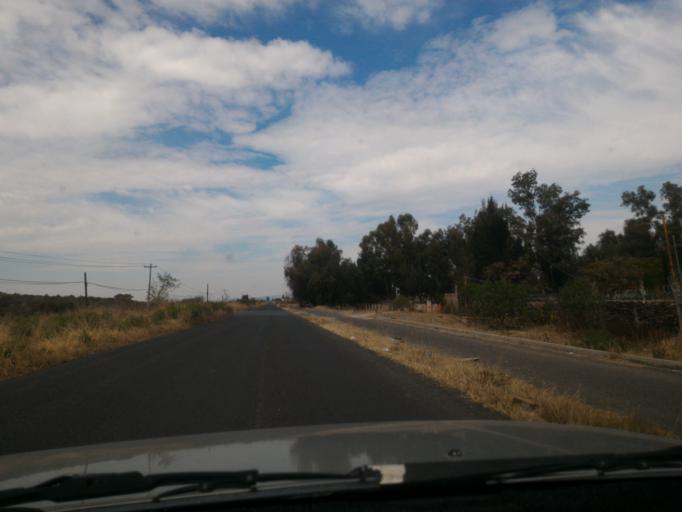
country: MX
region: Guanajuato
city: Ciudad Manuel Doblado
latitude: 20.7483
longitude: -101.9609
